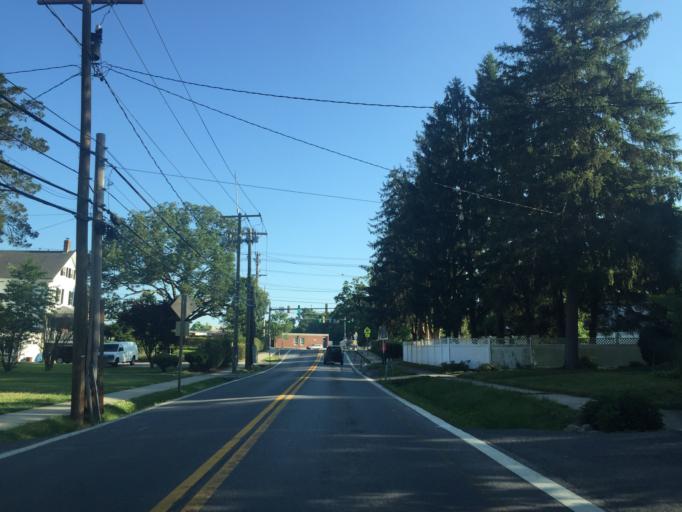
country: US
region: Maryland
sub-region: Baltimore County
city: Catonsville
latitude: 39.2679
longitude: -76.7457
